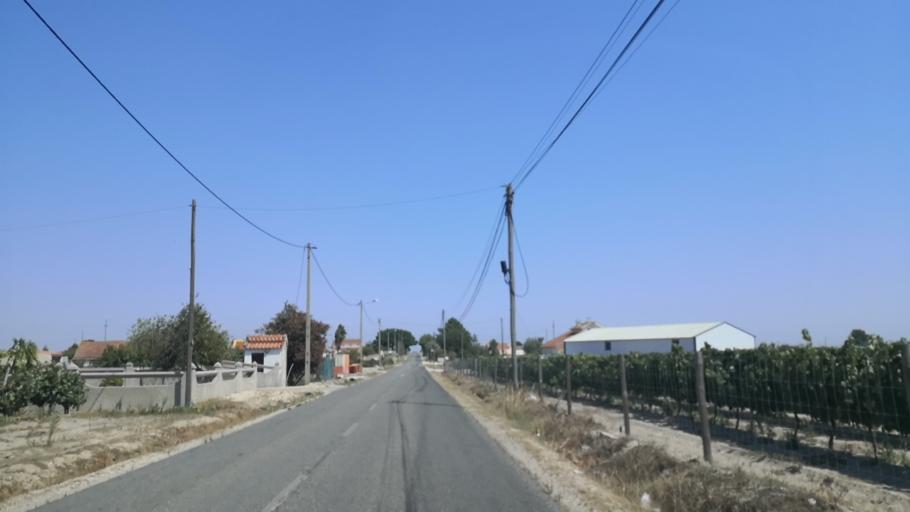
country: PT
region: Setubal
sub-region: Palmela
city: Palmela
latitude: 38.6053
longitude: -8.8358
